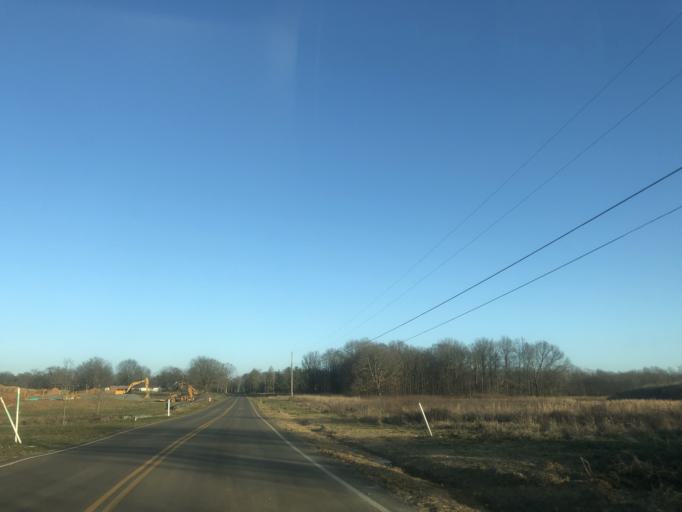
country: US
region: Tennessee
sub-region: Sumner County
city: White House
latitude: 36.4814
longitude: -86.7058
